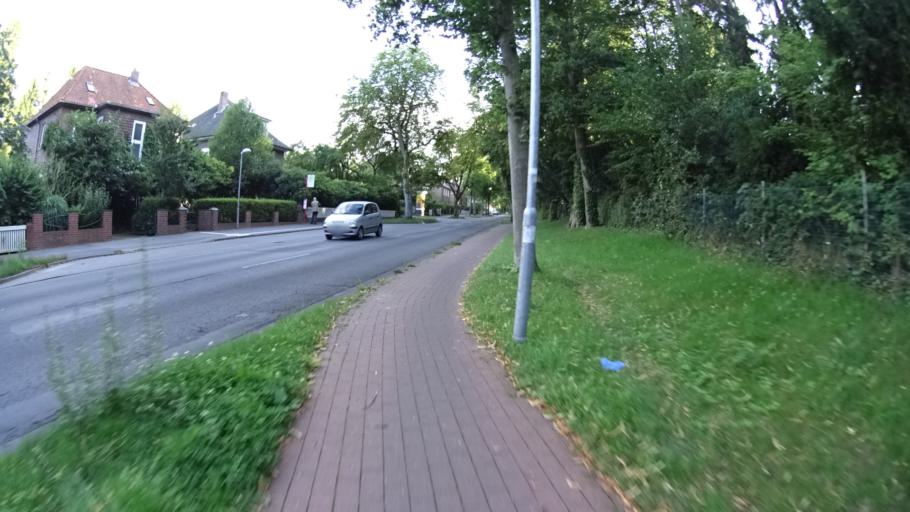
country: DE
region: Lower Saxony
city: Lueneburg
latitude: 53.2359
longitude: 10.3980
